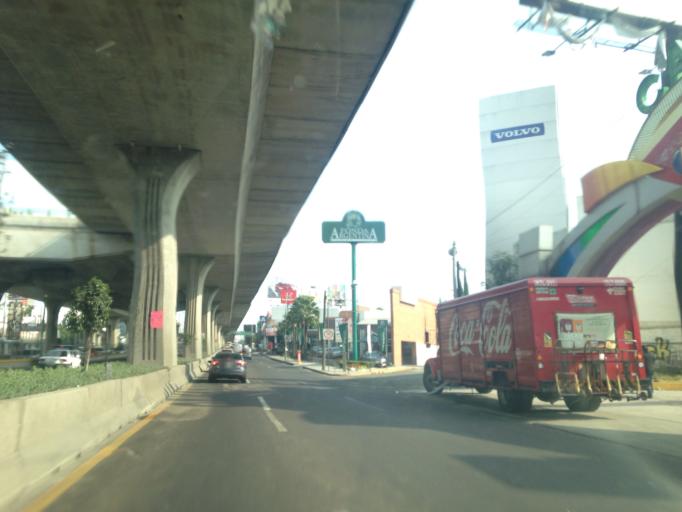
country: MX
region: Mexico
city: Naucalpan de Juarez
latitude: 19.4831
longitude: -99.2339
